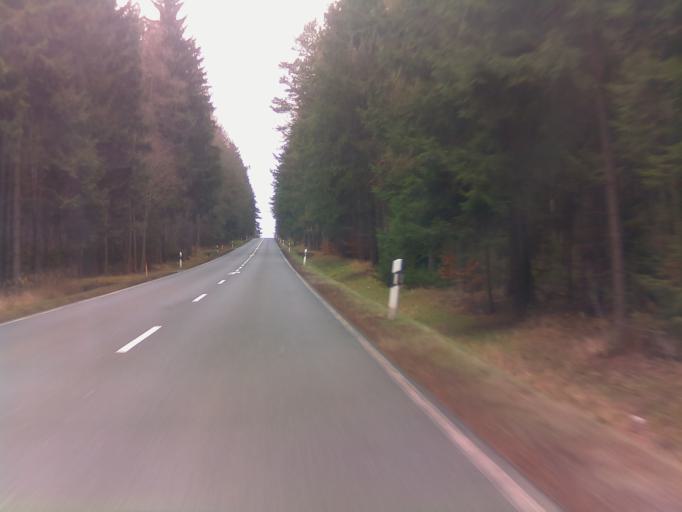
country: DE
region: Saxony
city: Pausa
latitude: 50.6133
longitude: 11.9966
